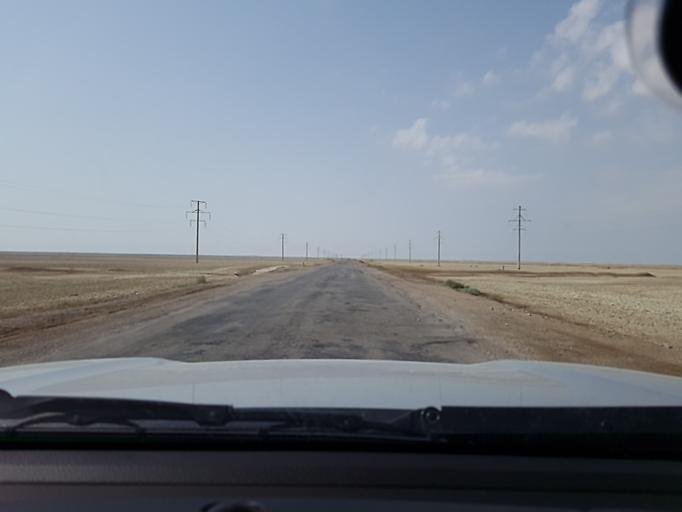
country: TM
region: Balkan
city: Gumdag
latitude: 39.0742
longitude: 54.5846
